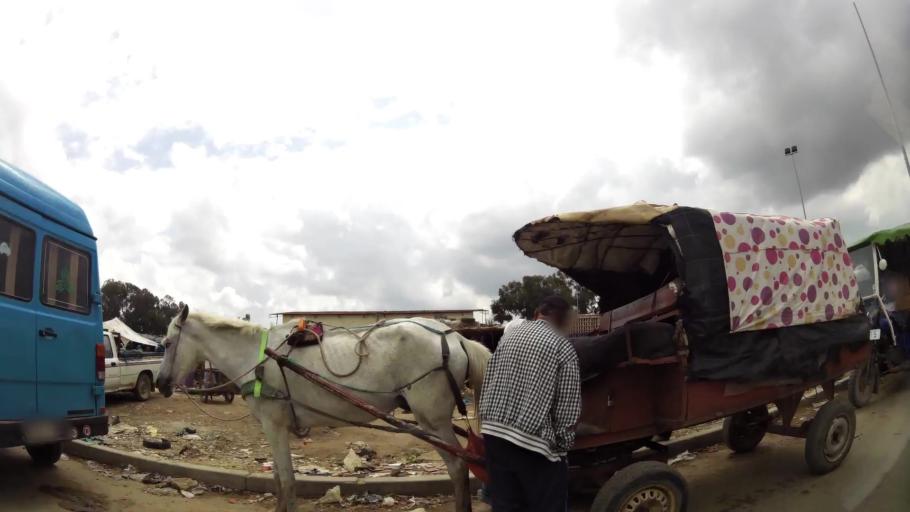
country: MA
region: Rabat-Sale-Zemmour-Zaer
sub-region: Khemisset
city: Tiflet
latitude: 33.8906
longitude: -6.3158
